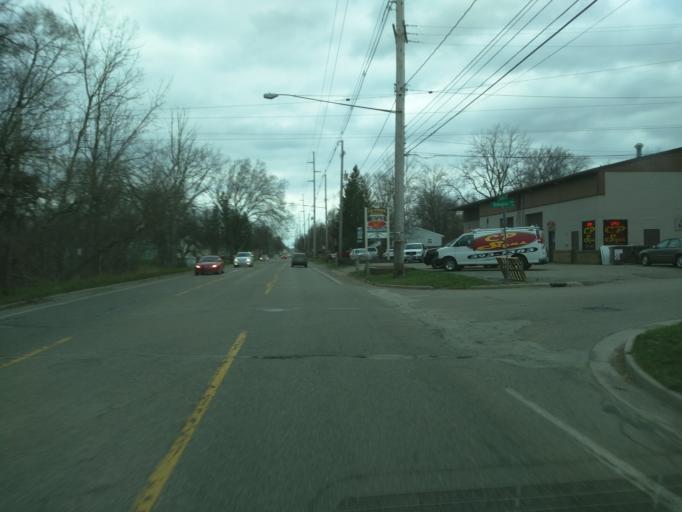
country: US
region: Michigan
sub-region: Ingham County
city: Lansing
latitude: 42.6949
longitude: -84.5234
